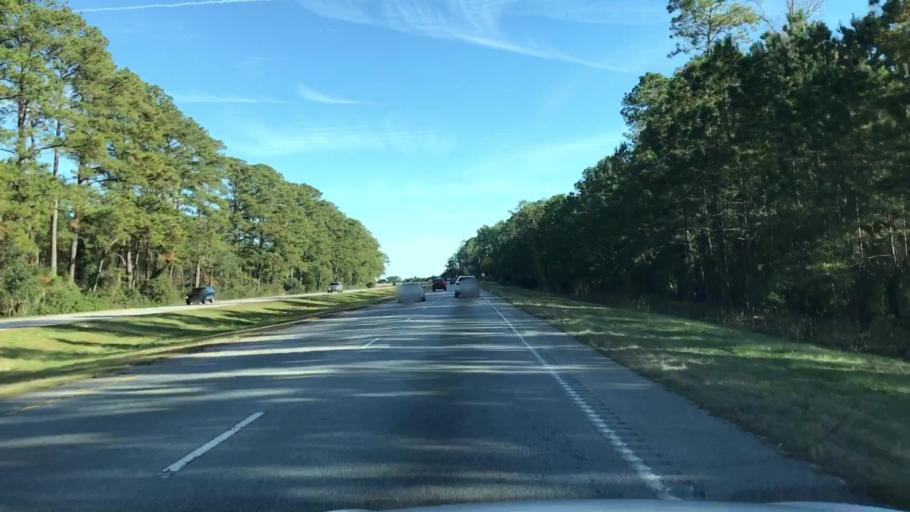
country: US
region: South Carolina
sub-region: Beaufort County
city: Shell Point
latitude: 32.3712
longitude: -80.8177
